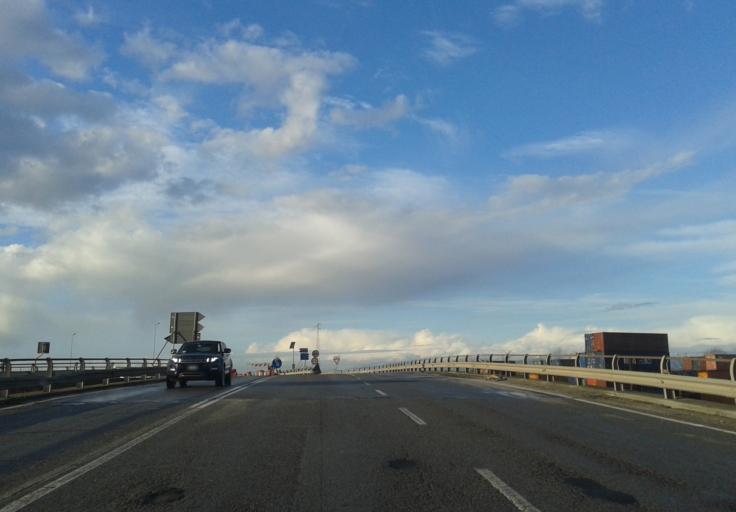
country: IT
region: Tuscany
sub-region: Provincia di Livorno
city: Livorno
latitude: 43.5862
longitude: 10.3241
